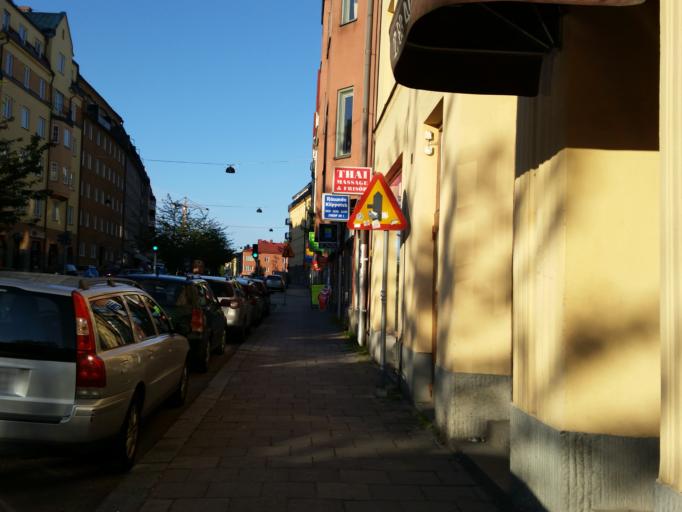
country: SE
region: Stockholm
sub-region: Solna Kommun
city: Solna
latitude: 59.3649
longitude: 17.9956
